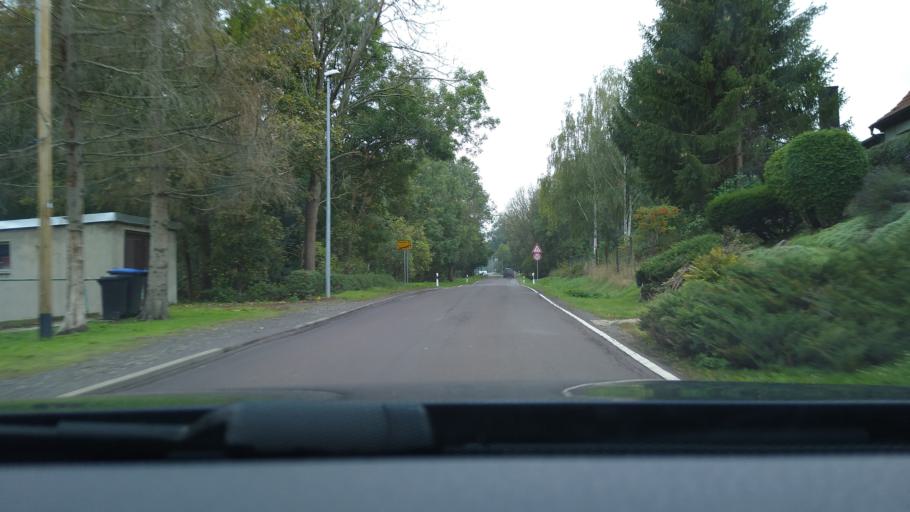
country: DE
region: Saxony-Anhalt
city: Polleben
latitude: 51.6017
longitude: 11.6138
